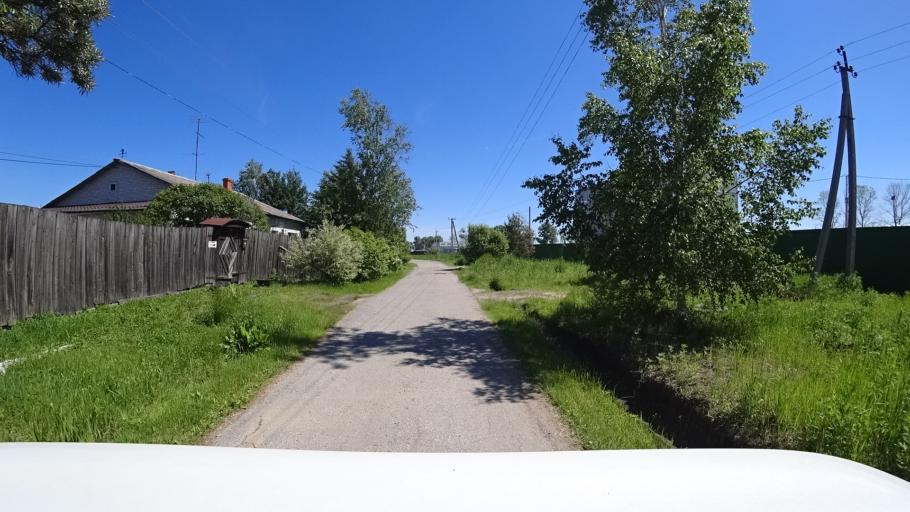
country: RU
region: Khabarovsk Krai
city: Topolevo
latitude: 48.5019
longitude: 135.1741
